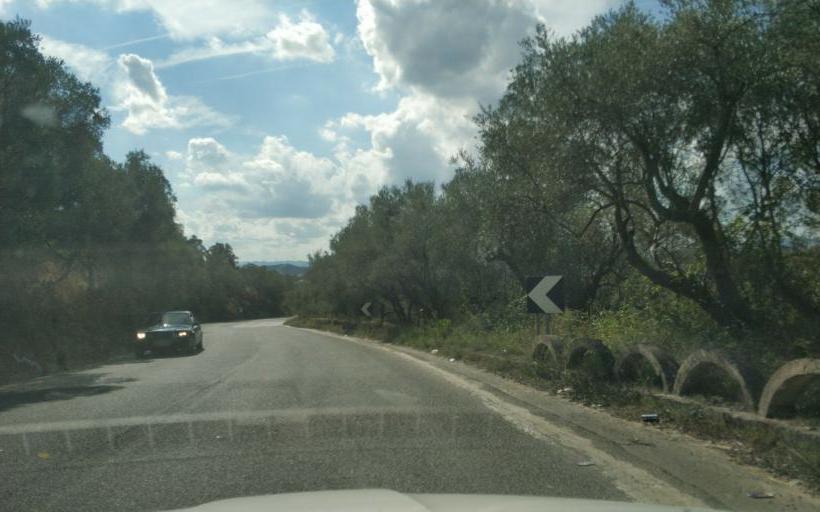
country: AL
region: Durres
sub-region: Rrethi i Krujes
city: Kruje
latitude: 41.4845
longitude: 19.7661
